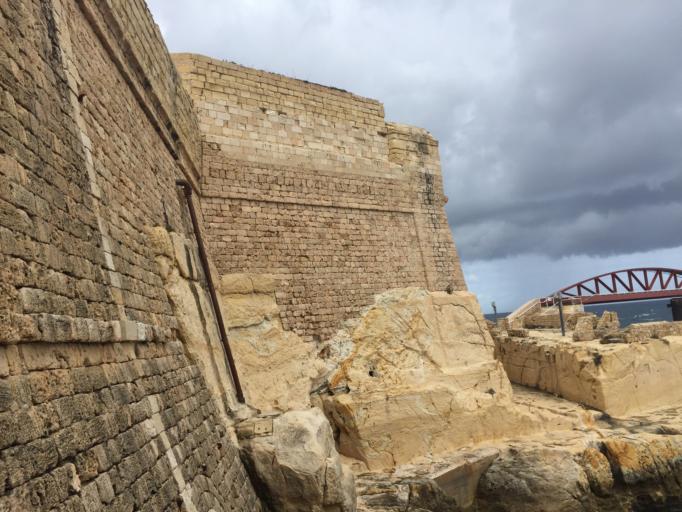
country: MT
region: Il-Belt Valletta
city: Valletta
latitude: 35.9021
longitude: 14.5196
